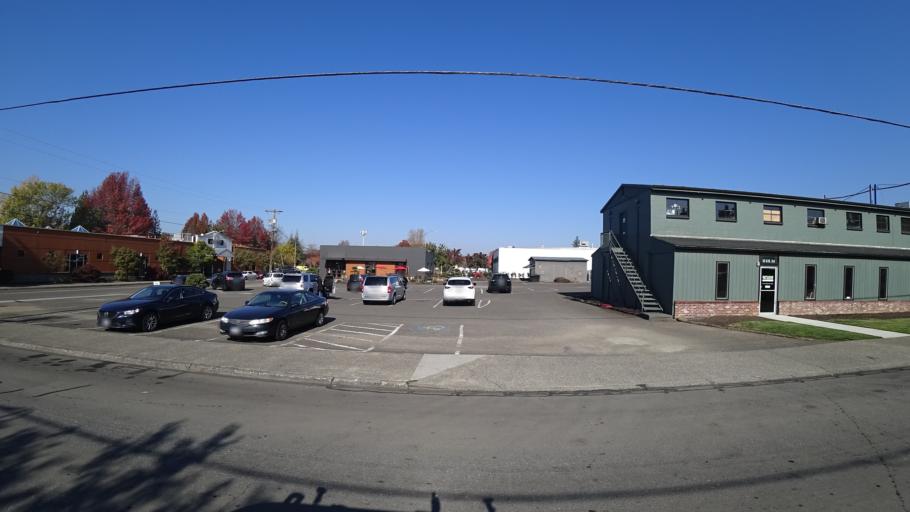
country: US
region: Oregon
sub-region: Multnomah County
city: Gresham
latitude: 45.4997
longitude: -122.4321
